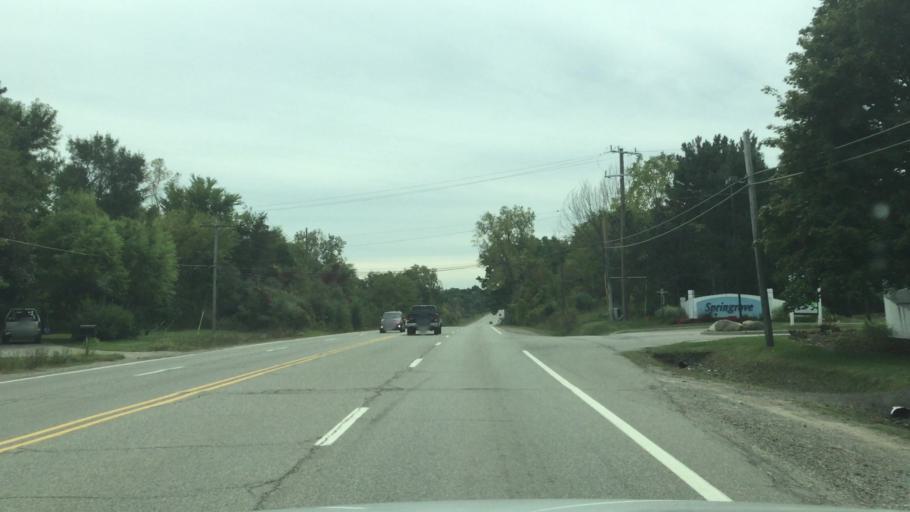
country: US
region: Michigan
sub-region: Oakland County
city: Ortonville
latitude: 42.7844
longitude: -83.5036
